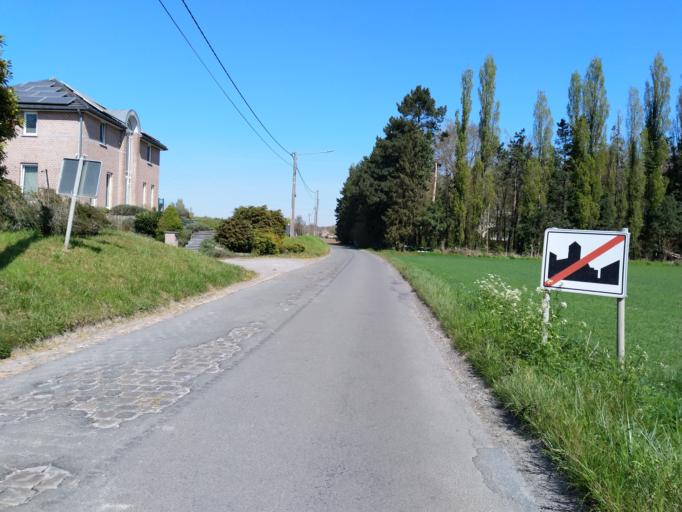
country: BE
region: Wallonia
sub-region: Province du Hainaut
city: Mons
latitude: 50.4811
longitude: 4.0113
